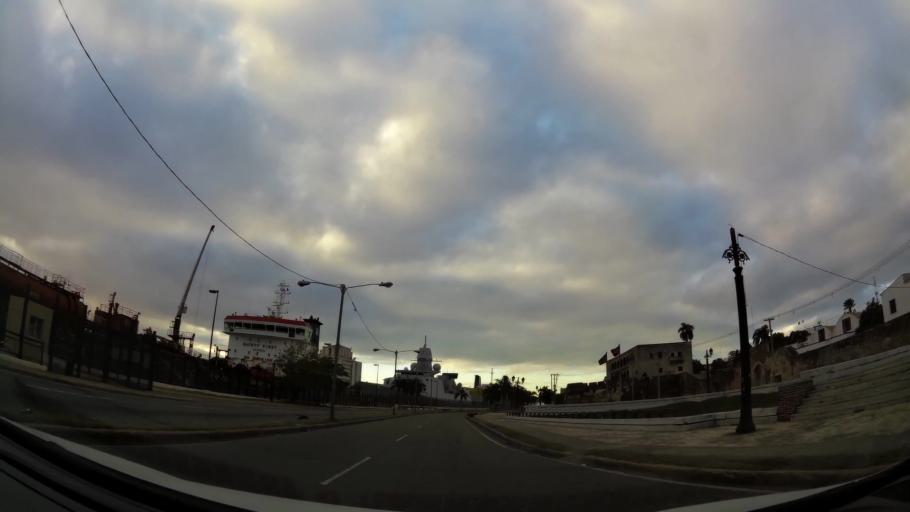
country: DO
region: Nacional
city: San Carlos
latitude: 18.4788
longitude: -69.8827
